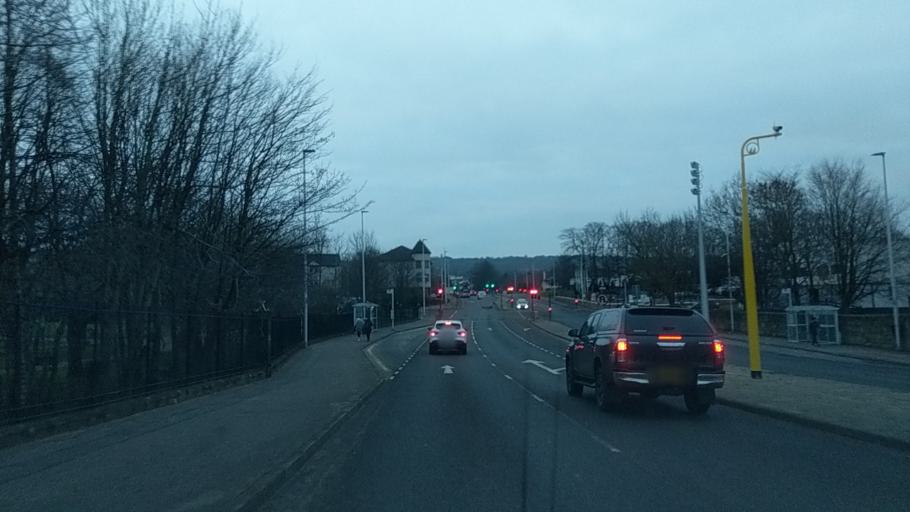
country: GB
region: Scotland
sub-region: South Lanarkshire
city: Rutherglen
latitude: 55.8214
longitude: -4.2157
